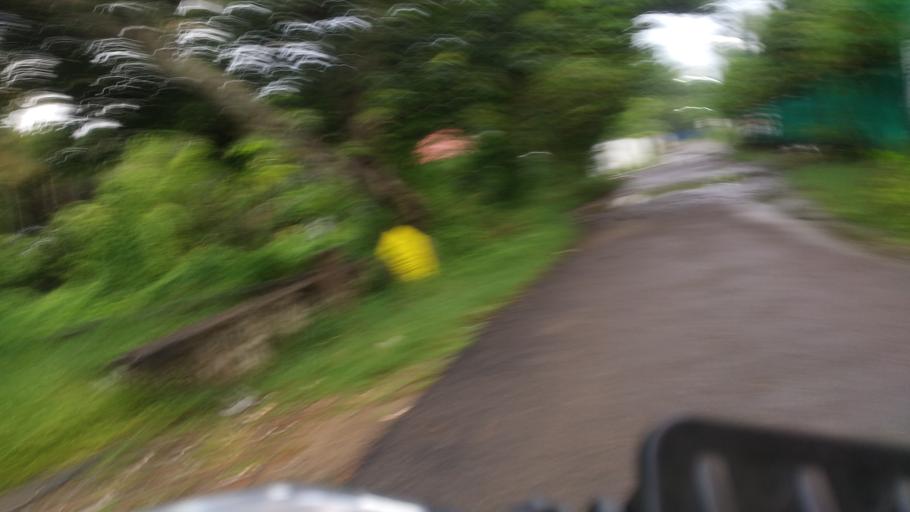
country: IN
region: Kerala
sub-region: Ernakulam
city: Cochin
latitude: 10.0125
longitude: 76.2171
